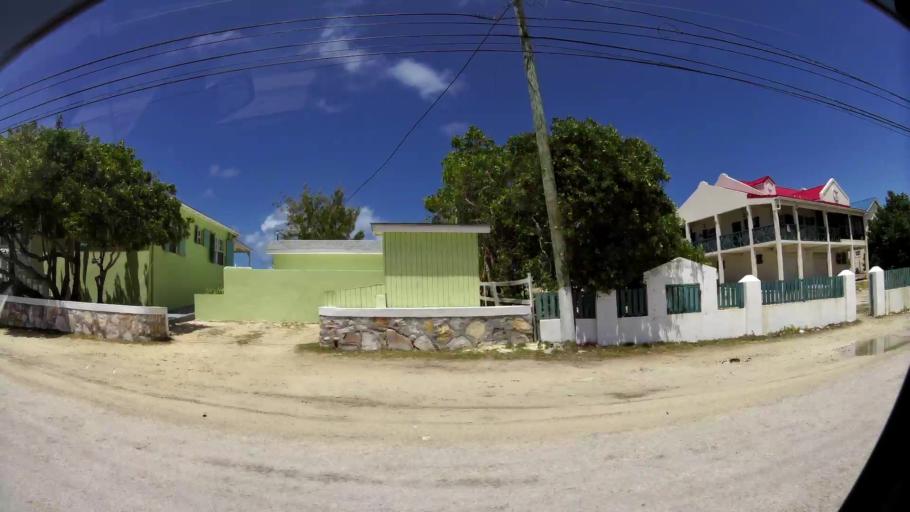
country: TC
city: Cockburn Town
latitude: 21.4547
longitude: -71.1492
